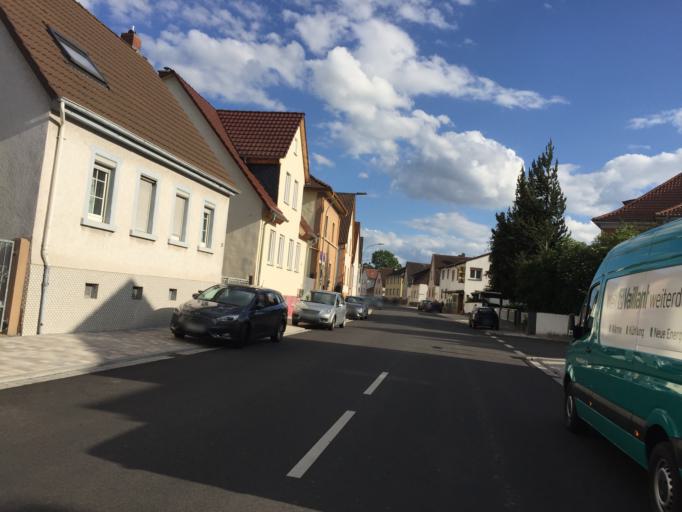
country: DE
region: Hesse
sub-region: Regierungsbezirk Darmstadt
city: Karben
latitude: 50.2298
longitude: 8.7730
